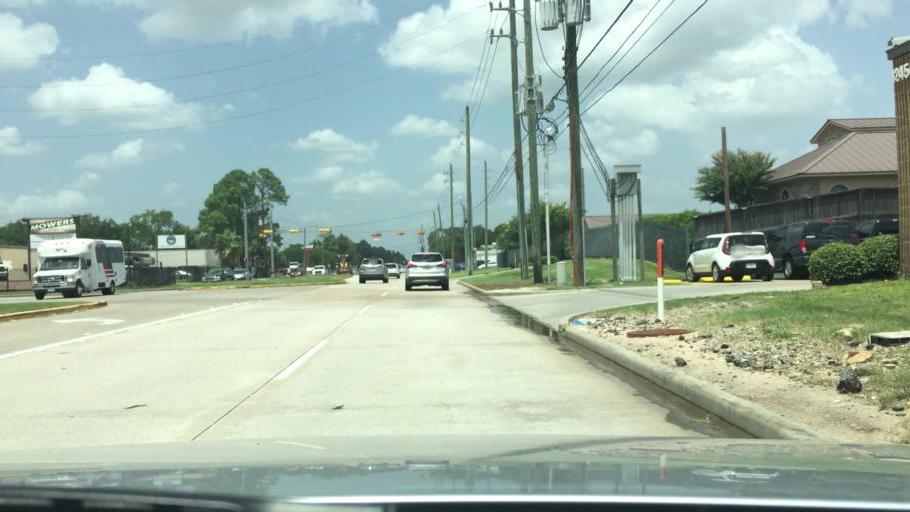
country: US
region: Texas
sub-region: Harris County
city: Hudson
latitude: 29.9616
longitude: -95.5285
